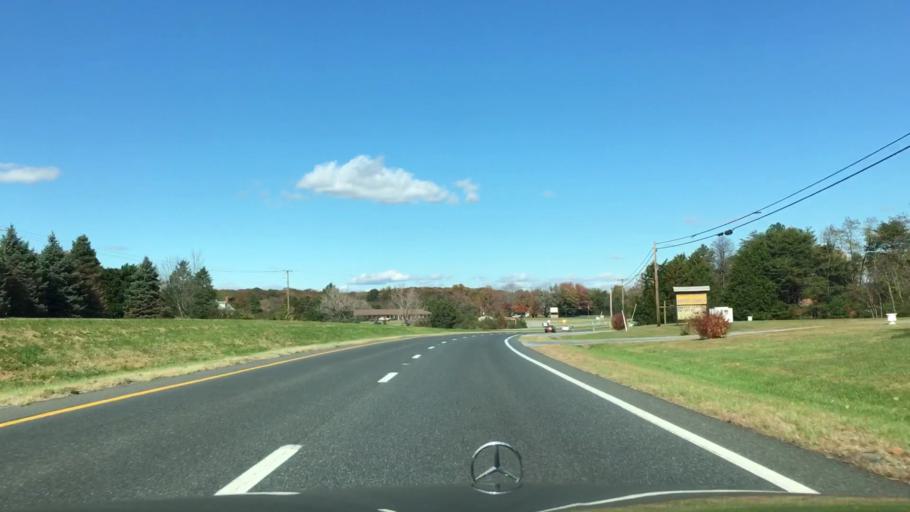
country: US
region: Virginia
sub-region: Campbell County
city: Rustburg
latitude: 37.2456
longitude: -79.1880
